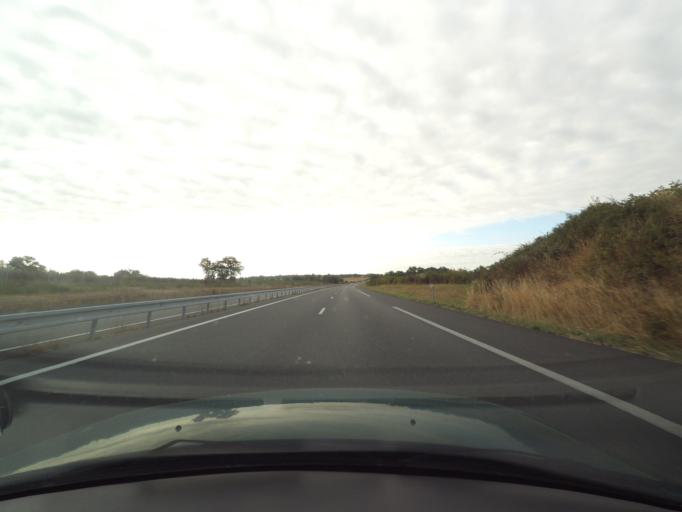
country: FR
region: Poitou-Charentes
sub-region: Departement des Deux-Sevres
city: Saint-Pierre-des-Echaubrognes
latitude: 46.9626
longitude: -0.7889
